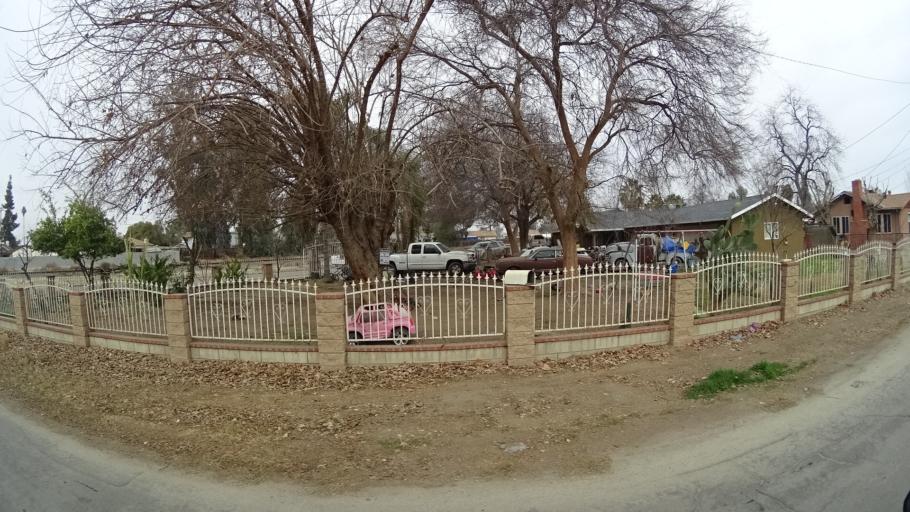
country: US
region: California
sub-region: Kern County
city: Bakersfield
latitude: 35.3420
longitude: -118.9992
